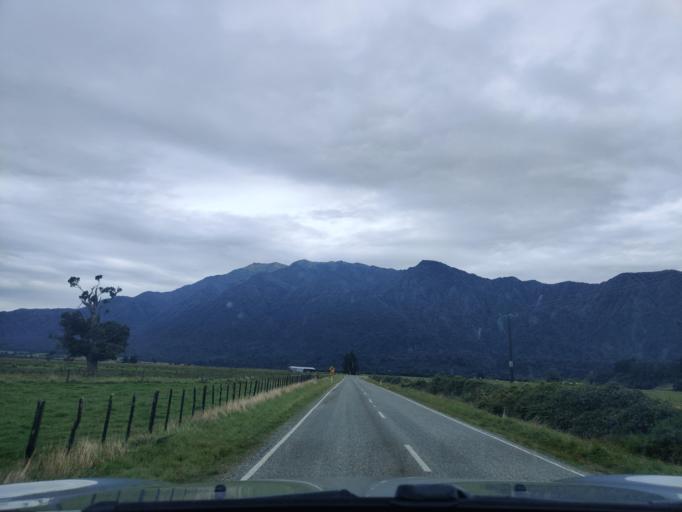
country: NZ
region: West Coast
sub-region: Westland District
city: Hokitika
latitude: -43.1534
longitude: 170.6071
